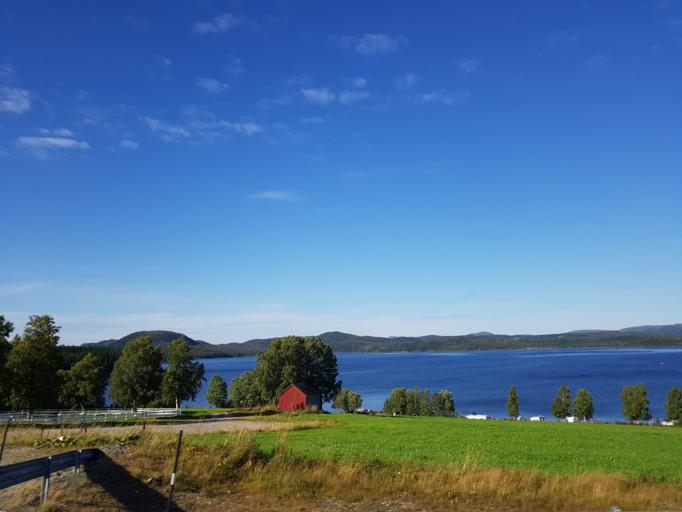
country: NO
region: Sor-Trondelag
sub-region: Trondheim
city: Trondheim
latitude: 63.6163
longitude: 10.2332
